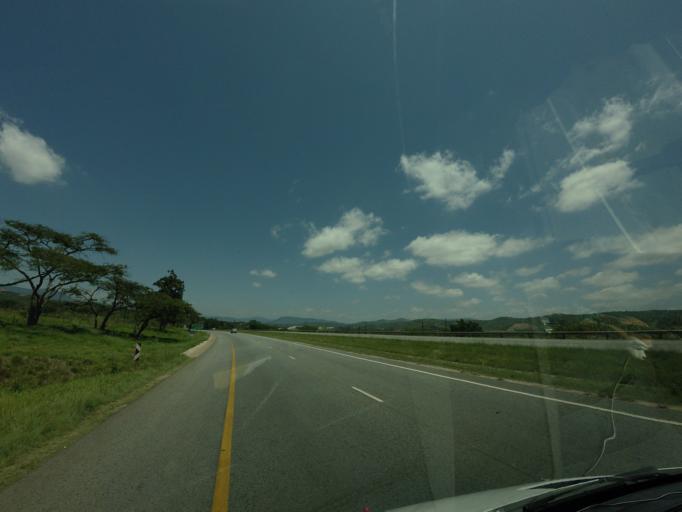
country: ZA
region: Mpumalanga
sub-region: Ehlanzeni District
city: Nelspruit
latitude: -25.4451
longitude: 30.8930
